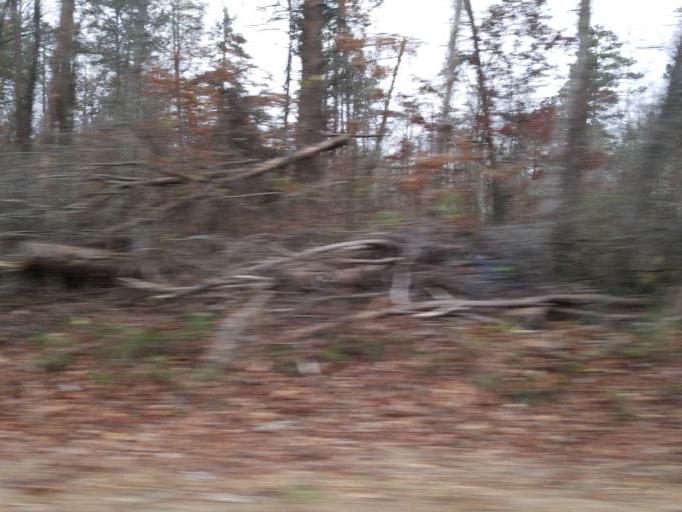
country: US
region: Georgia
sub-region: Dawson County
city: Dawsonville
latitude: 34.4317
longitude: -84.0563
